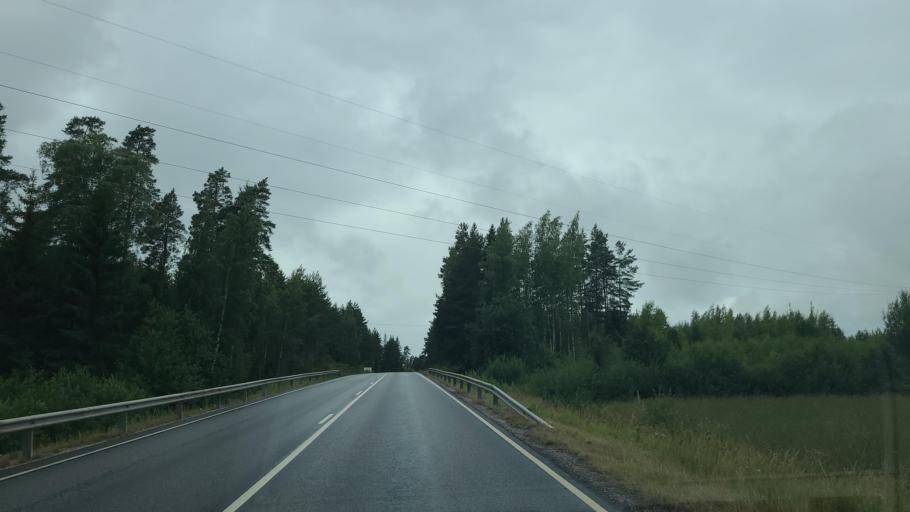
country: FI
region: Varsinais-Suomi
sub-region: Aboland-Turunmaa
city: Kimito
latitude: 60.2256
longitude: 22.6201
